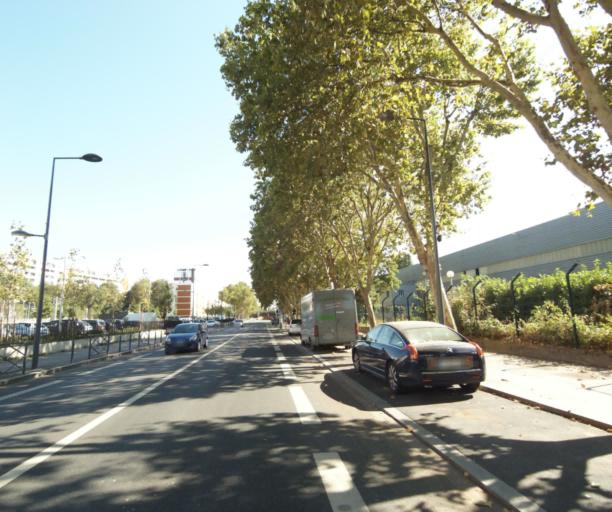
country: FR
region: Ile-de-France
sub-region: Departement des Hauts-de-Seine
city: Villeneuve-la-Garenne
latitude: 48.9334
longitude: 2.3252
